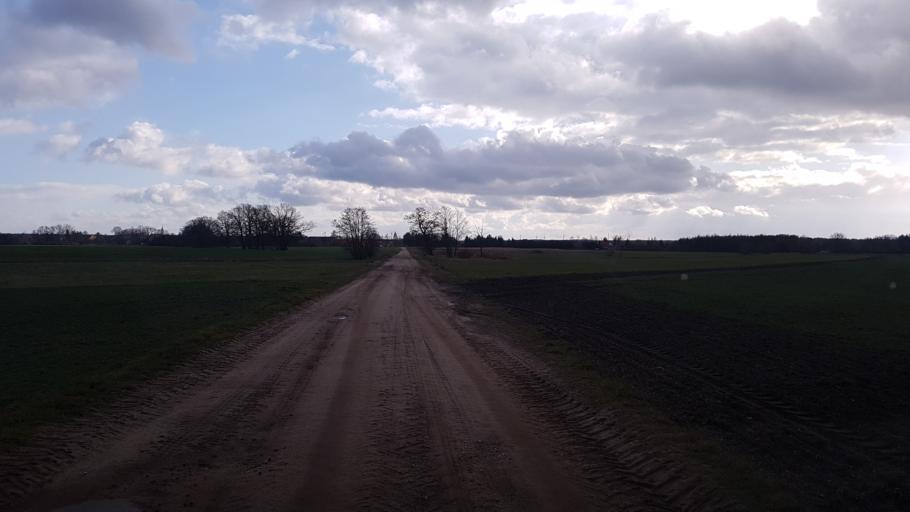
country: DE
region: Brandenburg
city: Sallgast
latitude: 51.6173
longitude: 13.8559
